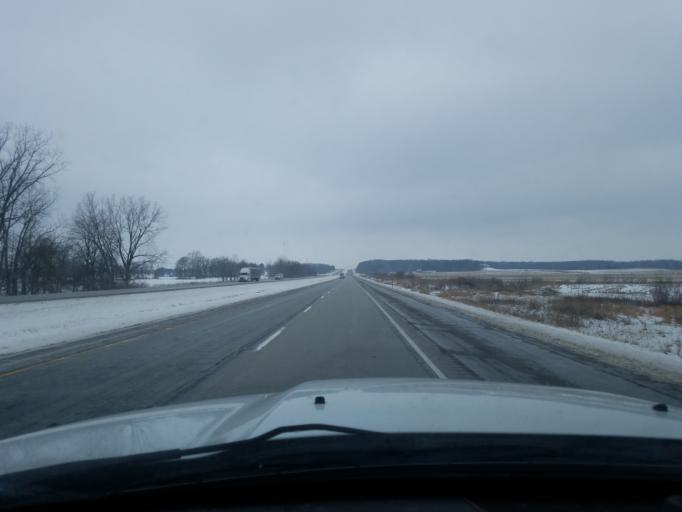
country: US
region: Indiana
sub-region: Fulton County
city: Rochester
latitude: 41.1009
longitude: -86.2397
